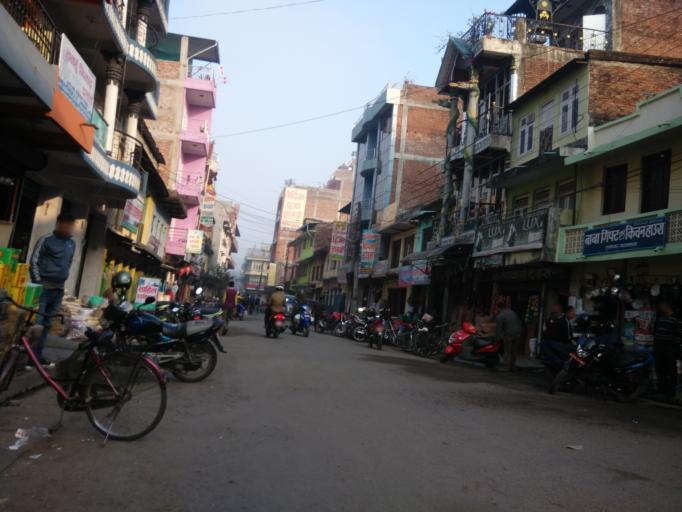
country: NP
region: Central Region
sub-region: Narayani Zone
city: Bharatpur
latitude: 27.6978
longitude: 84.4244
